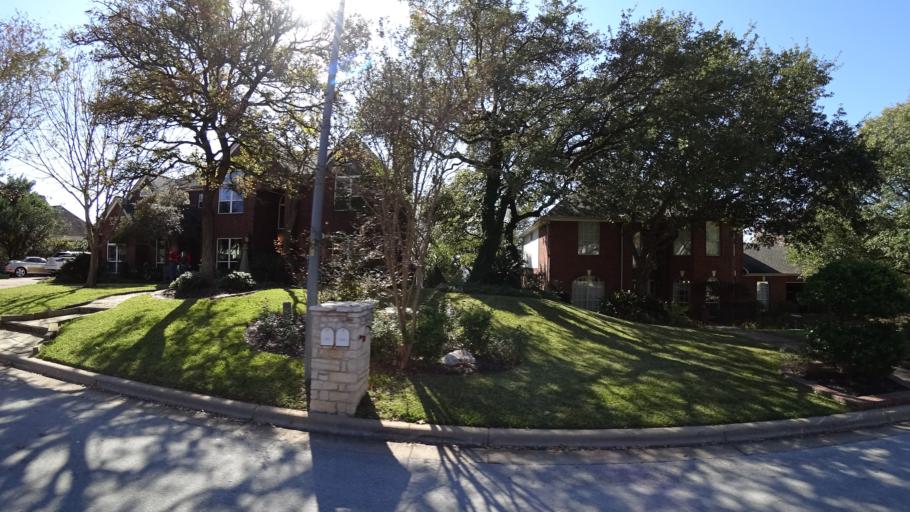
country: US
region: Texas
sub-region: Travis County
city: Lost Creek
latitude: 30.3758
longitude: -97.8526
